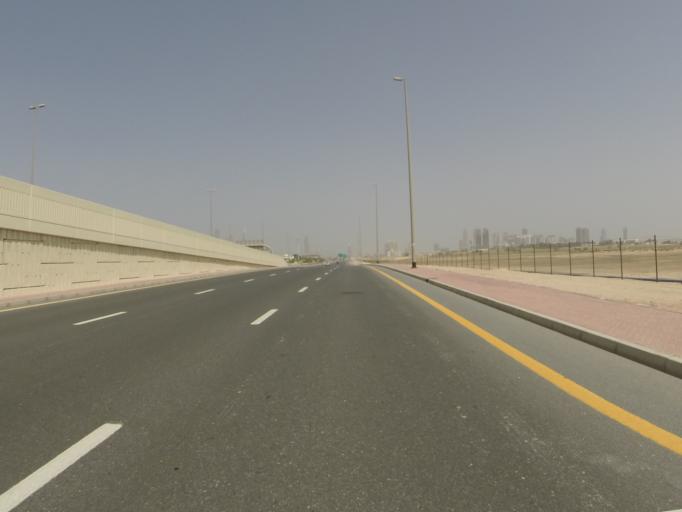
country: AE
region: Dubai
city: Dubai
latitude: 25.0697
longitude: 55.1916
